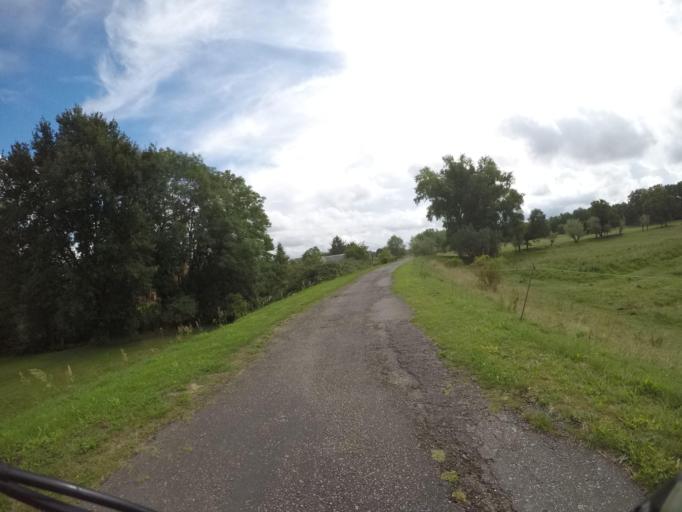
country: DE
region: Lower Saxony
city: Neu Darchau
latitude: 53.2492
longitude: 10.8790
